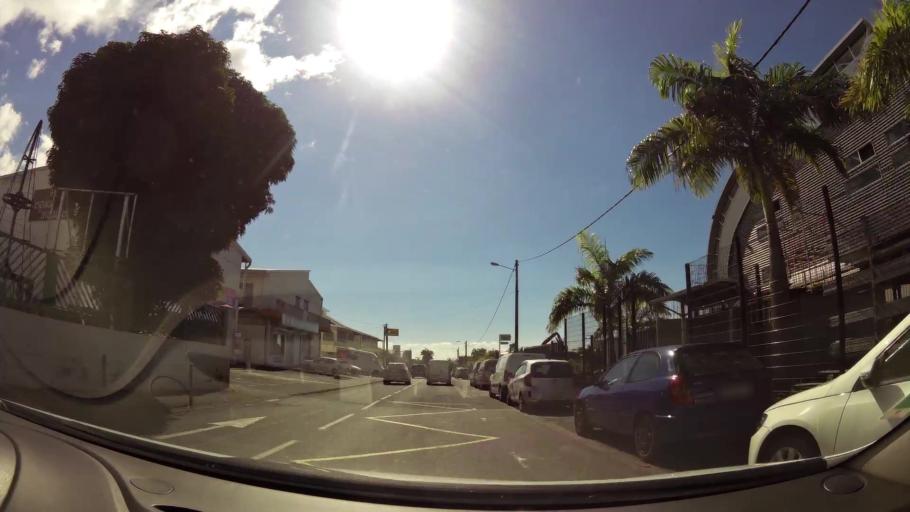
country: RE
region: Reunion
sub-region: Reunion
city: Saint-Denis
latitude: -20.8928
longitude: 55.4971
